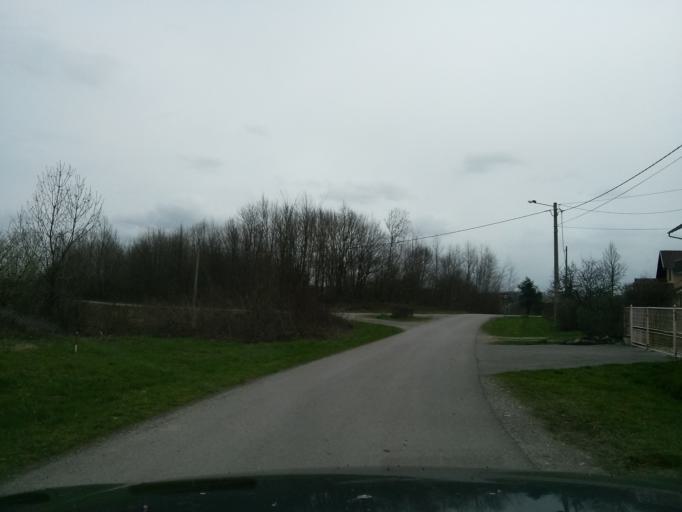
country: HR
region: Sisacko-Moslavacka
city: Gvozd
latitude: 45.2879
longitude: 15.9556
